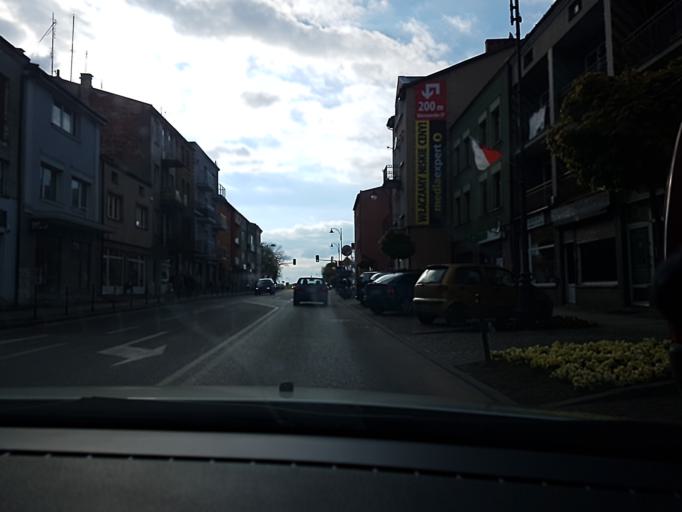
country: PL
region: Masovian Voivodeship
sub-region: Powiat sochaczewski
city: Sochaczew
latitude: 52.2291
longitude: 20.2401
